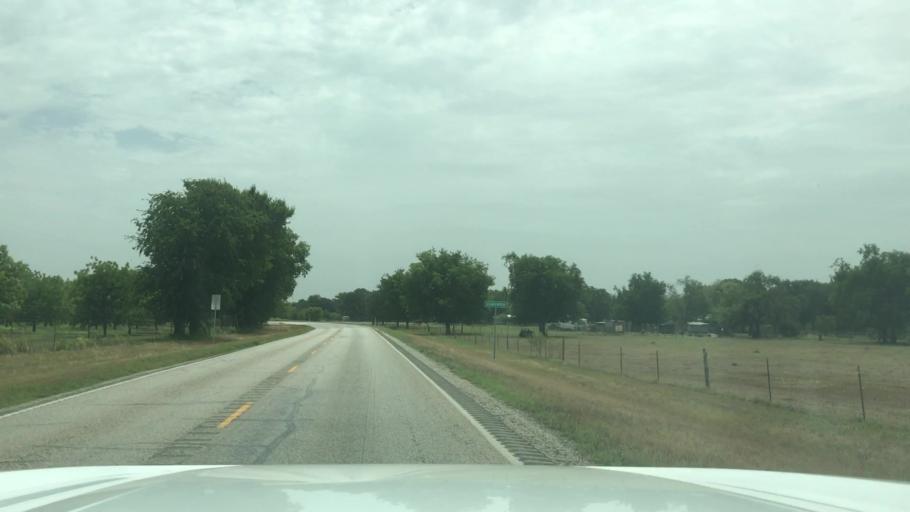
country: US
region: Texas
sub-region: Hamilton County
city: Hico
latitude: 32.0402
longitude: -98.1248
